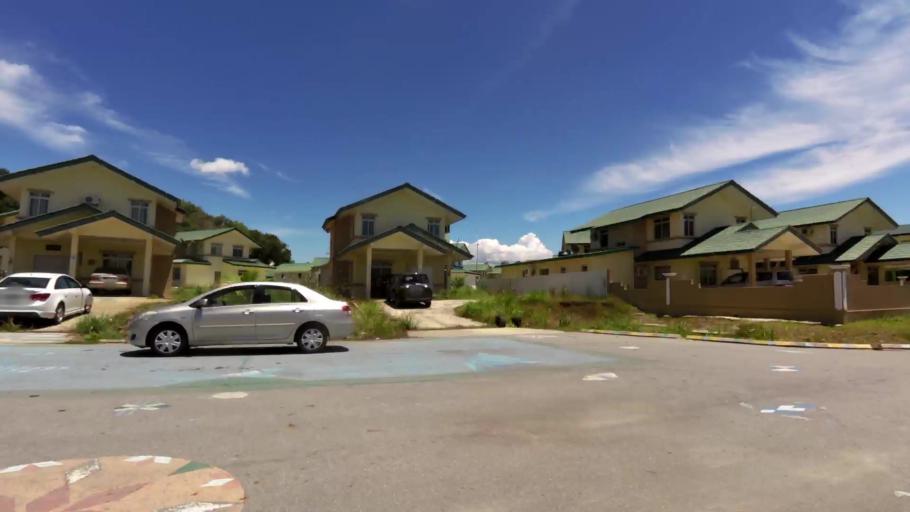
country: BN
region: Brunei and Muara
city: Bandar Seri Begawan
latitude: 5.0229
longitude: 115.0361
